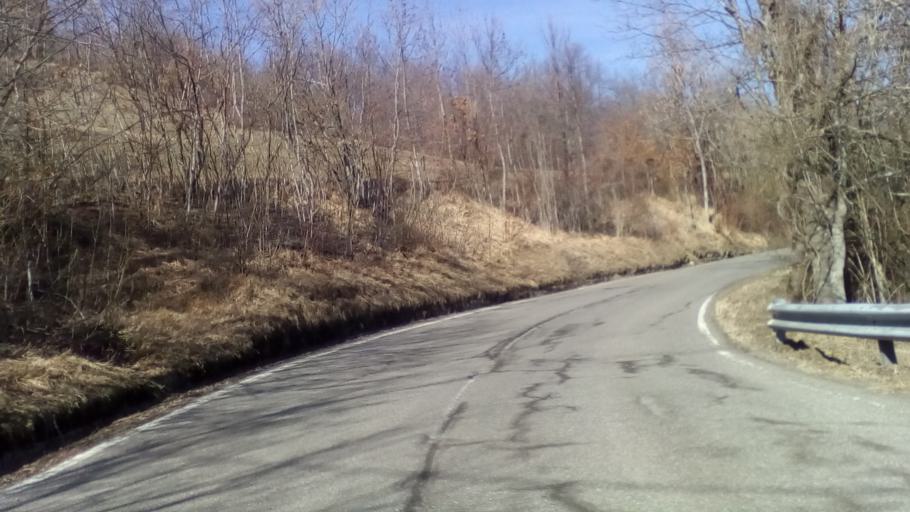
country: IT
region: Emilia-Romagna
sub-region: Provincia di Modena
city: Riolunato
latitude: 44.2417
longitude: 10.6339
